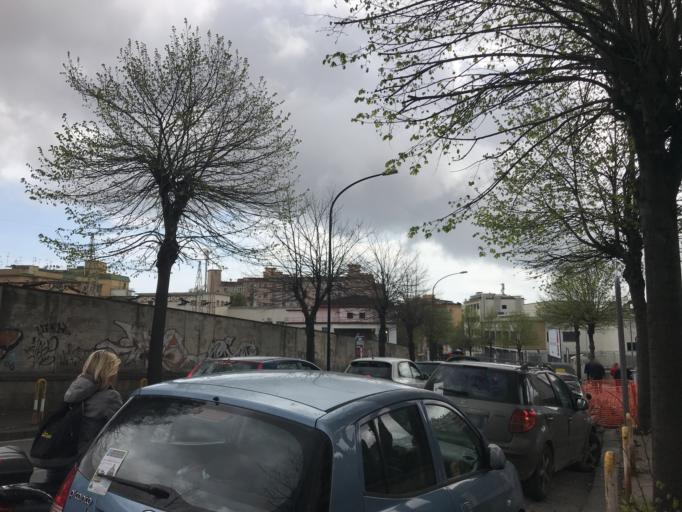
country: IT
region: Campania
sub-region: Provincia di Napoli
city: Napoli
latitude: 40.8565
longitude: 14.2247
